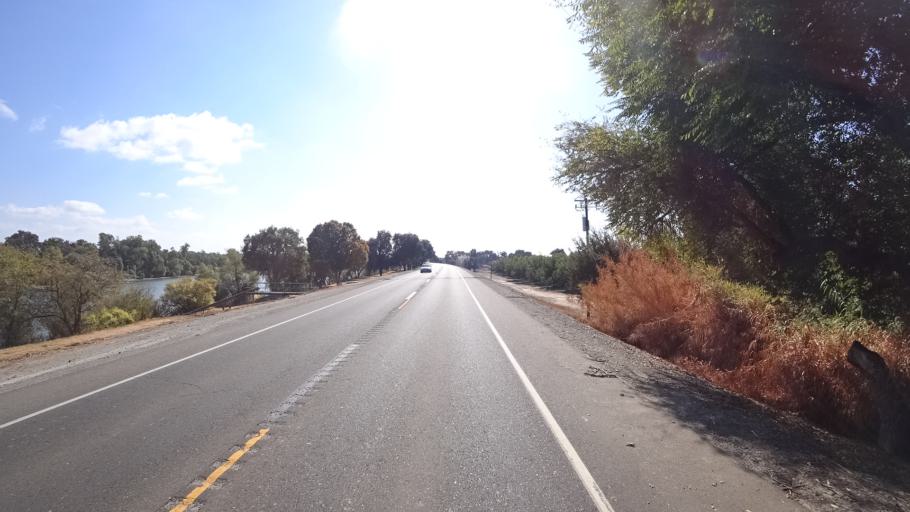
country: US
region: California
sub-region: Yolo County
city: West Sacramento
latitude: 38.6187
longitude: -121.5633
